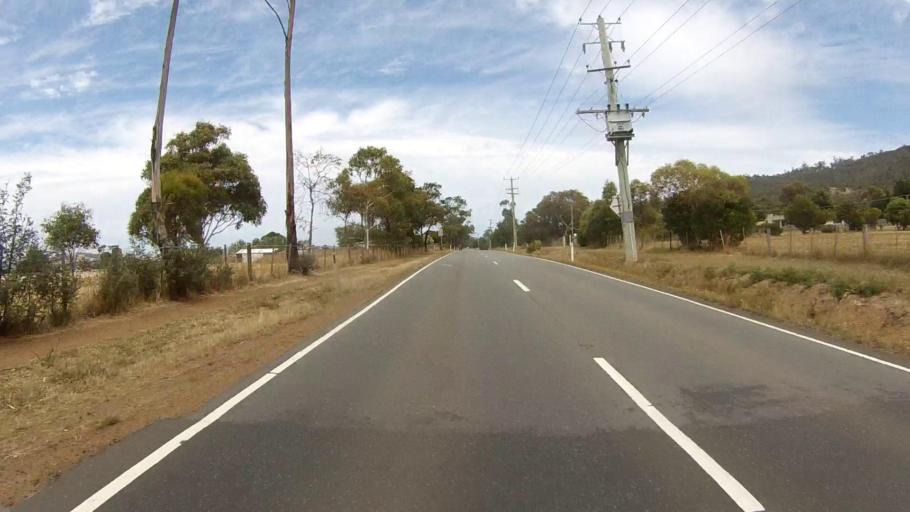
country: AU
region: Tasmania
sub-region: Clarence
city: Acton Park
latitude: -42.8884
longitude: 147.4829
